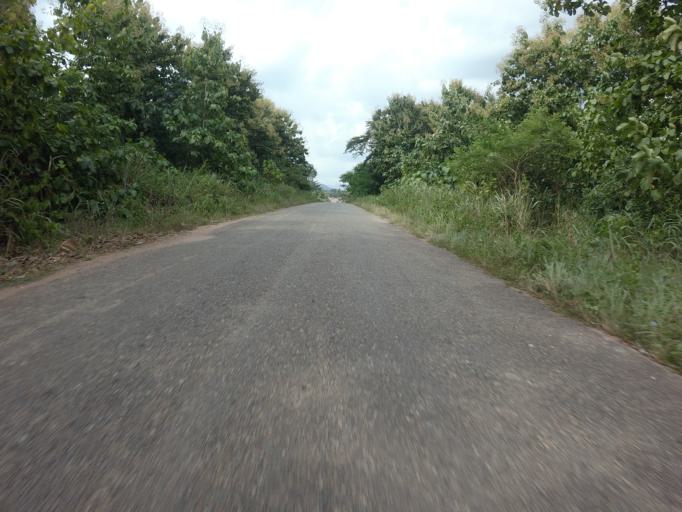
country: GH
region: Volta
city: Ho
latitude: 6.6679
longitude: 0.3522
